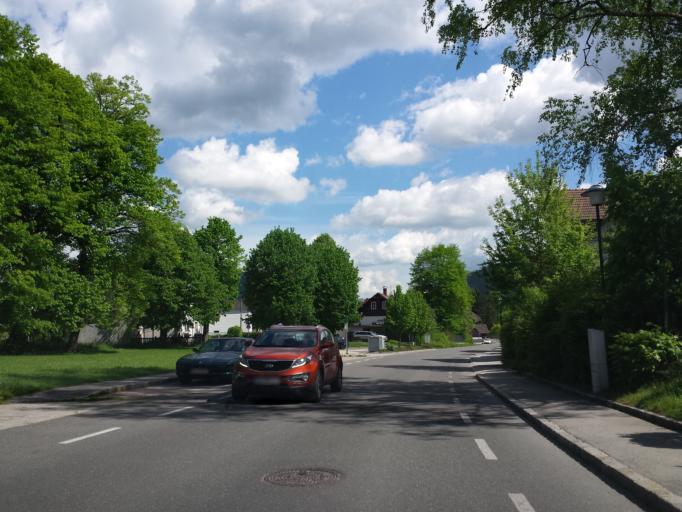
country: AT
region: Lower Austria
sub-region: Politischer Bezirk Wiener Neustadt
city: Pernitz
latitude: 47.9024
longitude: 15.9518
